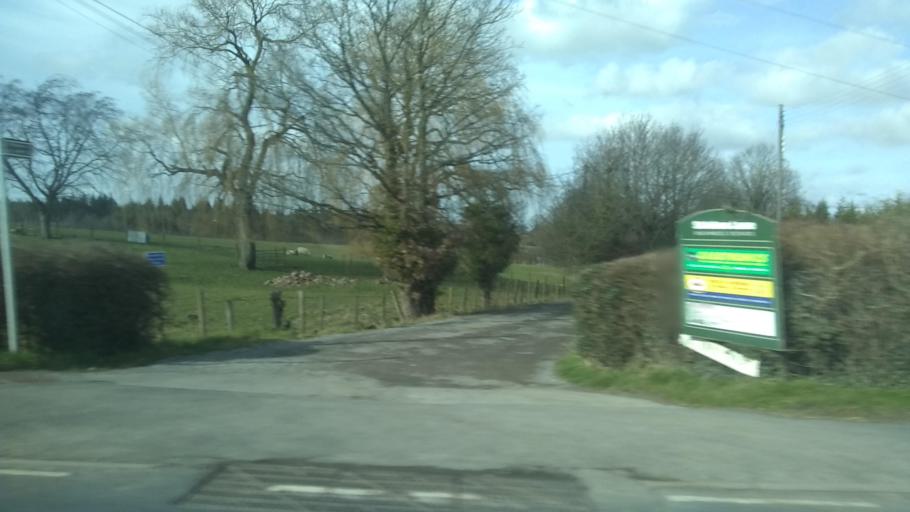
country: GB
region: England
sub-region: Worcestershire
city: Bewdley
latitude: 52.3650
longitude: -2.3581
